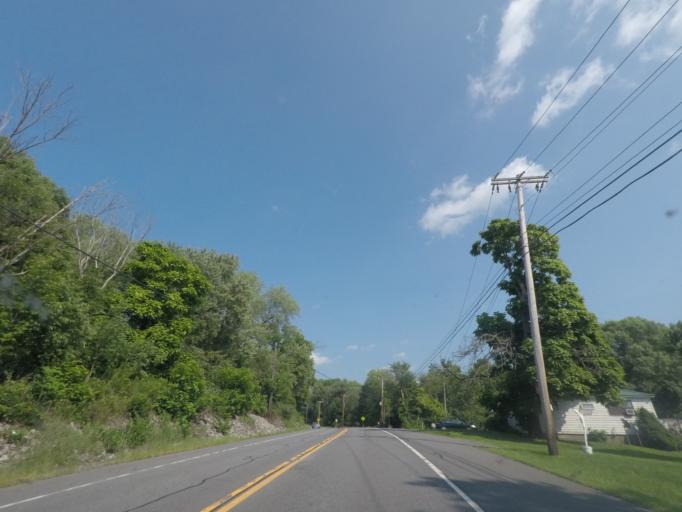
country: US
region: New York
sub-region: Rensselaer County
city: Nassau
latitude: 42.5284
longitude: -73.6510
